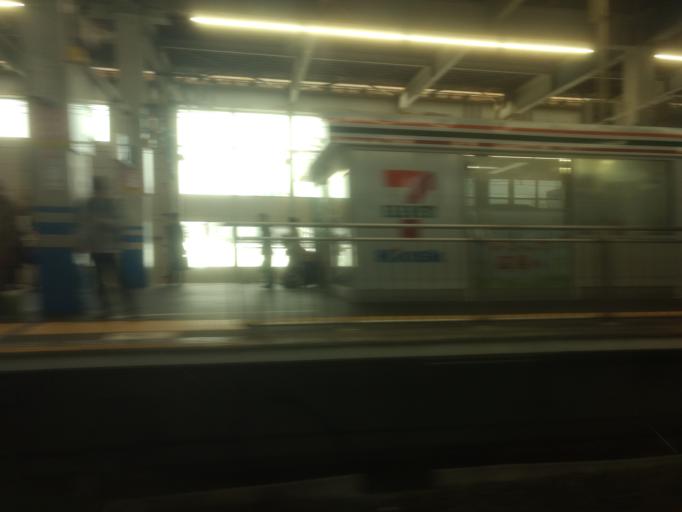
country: JP
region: Hiroshima
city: Hiroshima-shi
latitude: 34.3982
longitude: 132.4761
